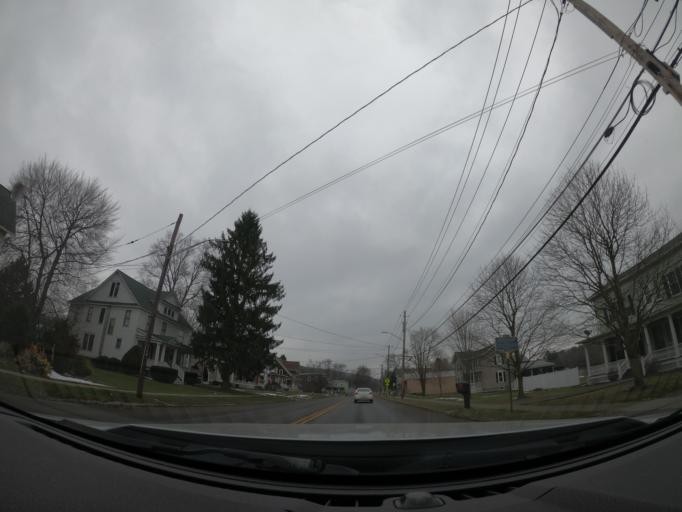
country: US
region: New York
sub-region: Cayuga County
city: Moravia
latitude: 42.6622
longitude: -76.4306
